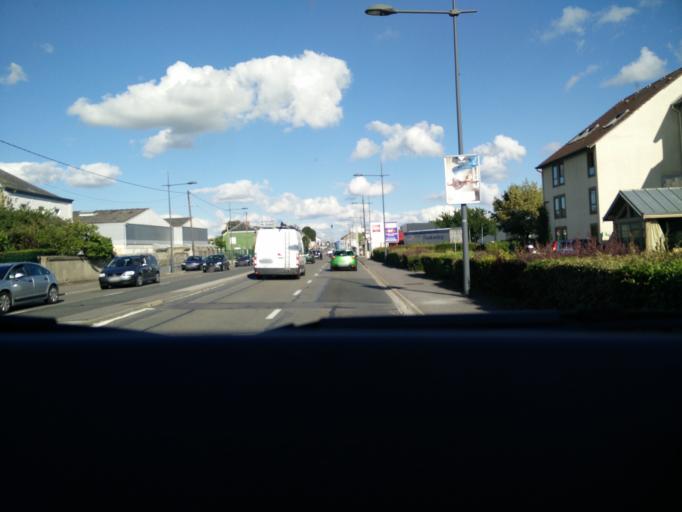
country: FR
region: Nord-Pas-de-Calais
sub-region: Departement du Nord
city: Maubeuge
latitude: 50.2818
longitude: 3.9559
